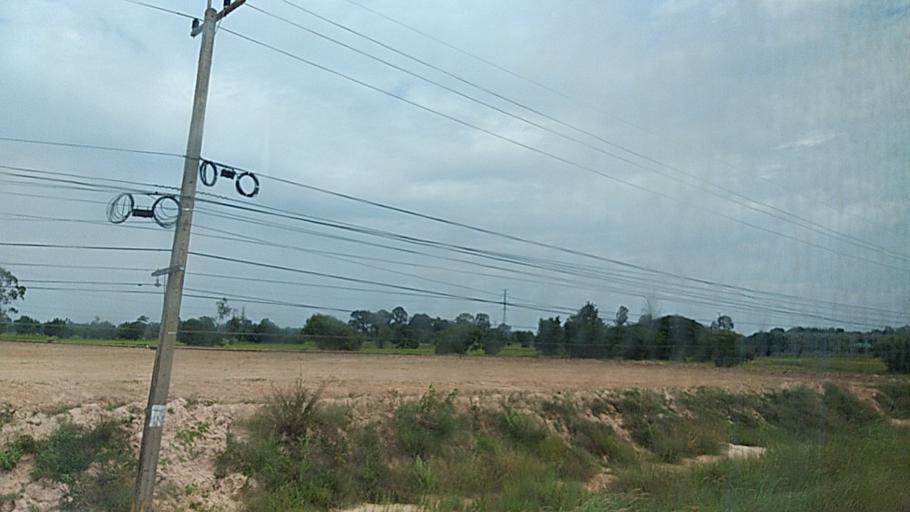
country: TH
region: Roi Et
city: Changhan
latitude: 16.1041
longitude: 103.5202
